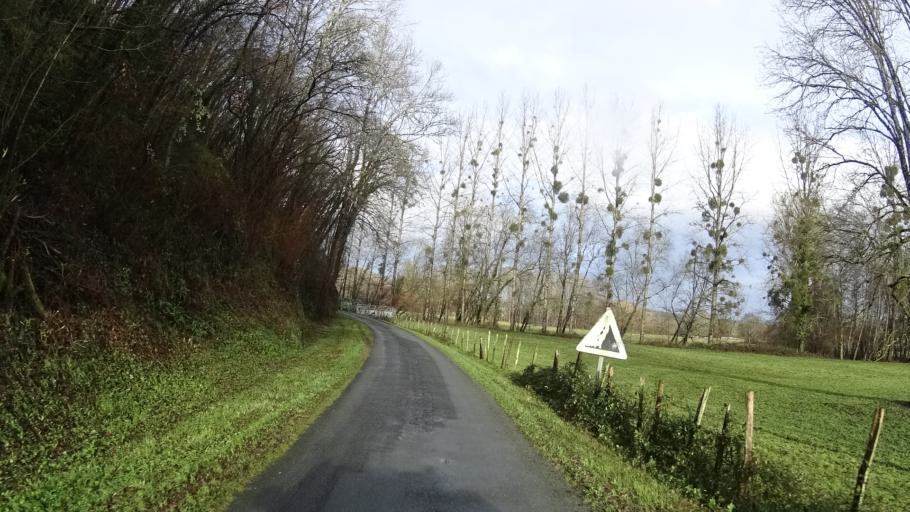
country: FR
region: Aquitaine
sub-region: Departement de la Dordogne
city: Thiviers
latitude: 45.3649
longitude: 0.9505
